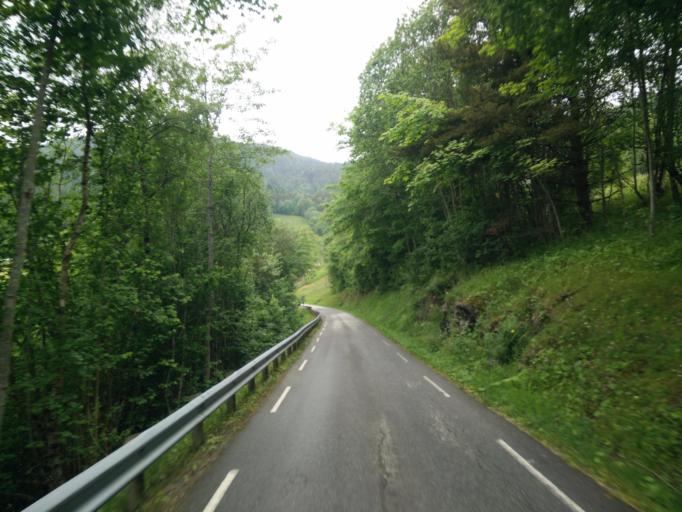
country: NO
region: More og Romsdal
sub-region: Kristiansund
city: Rensvik
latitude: 63.0217
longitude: 7.9490
